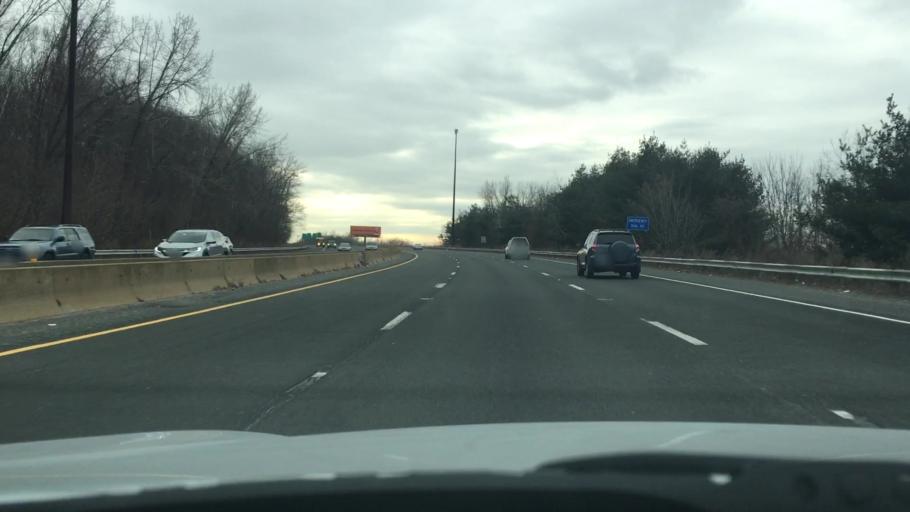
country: US
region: Massachusetts
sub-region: Hampden County
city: North Chicopee
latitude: 42.1757
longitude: -72.6094
